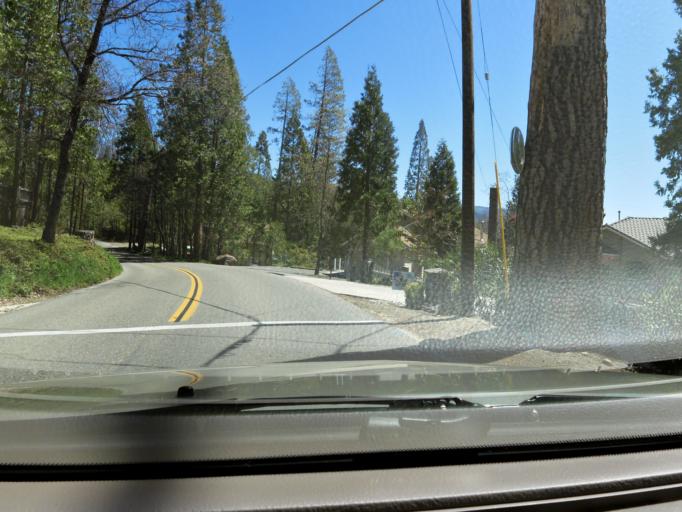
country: US
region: California
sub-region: Madera County
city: Oakhurst
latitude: 37.3213
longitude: -119.5649
